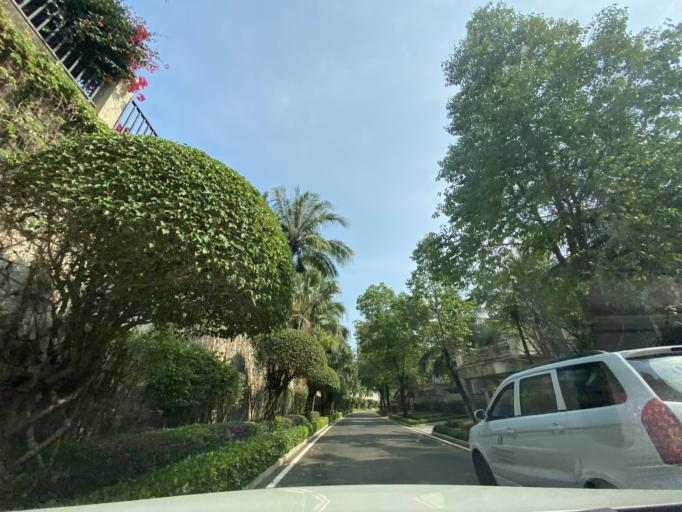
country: CN
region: Hainan
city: Yingzhou
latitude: 18.4129
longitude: 109.8433
